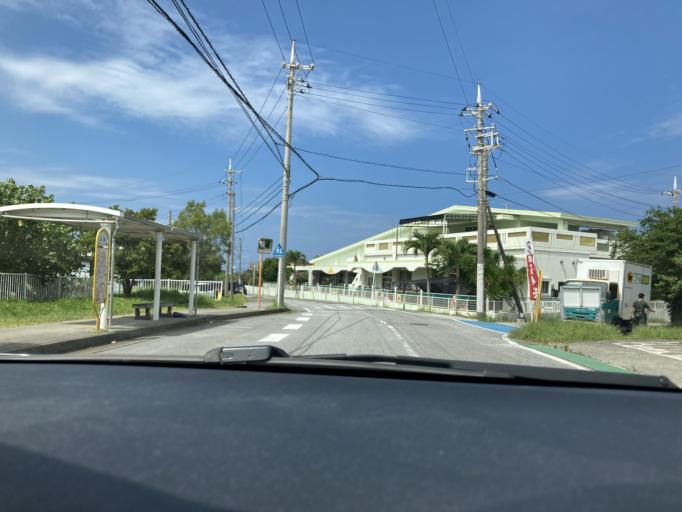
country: JP
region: Okinawa
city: Ishikawa
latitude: 26.4345
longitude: 127.7769
